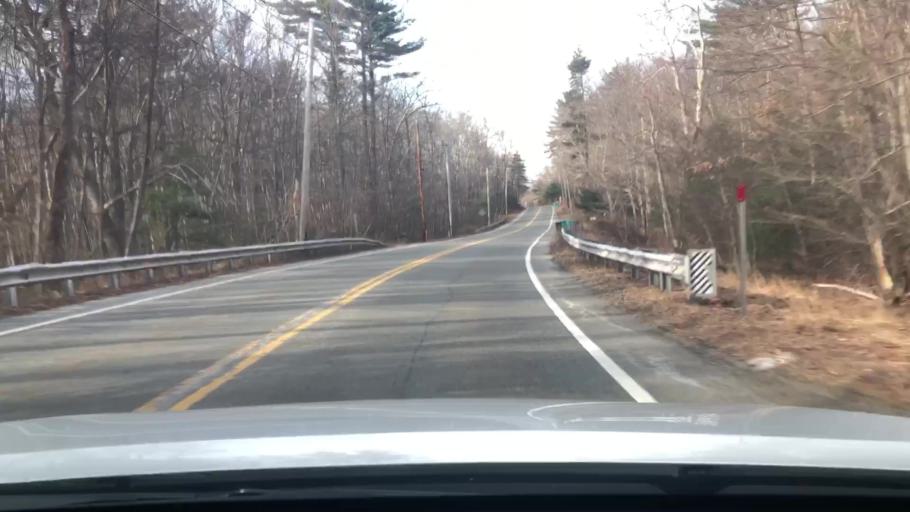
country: US
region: Massachusetts
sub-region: Worcester County
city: Upton
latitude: 42.1640
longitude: -71.5907
